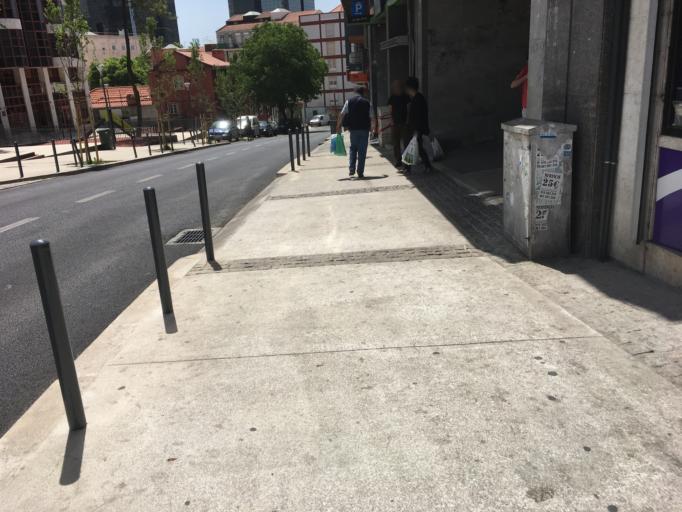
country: PT
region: Lisbon
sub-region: Lisbon
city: Lisbon
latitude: 38.7265
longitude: -9.1624
